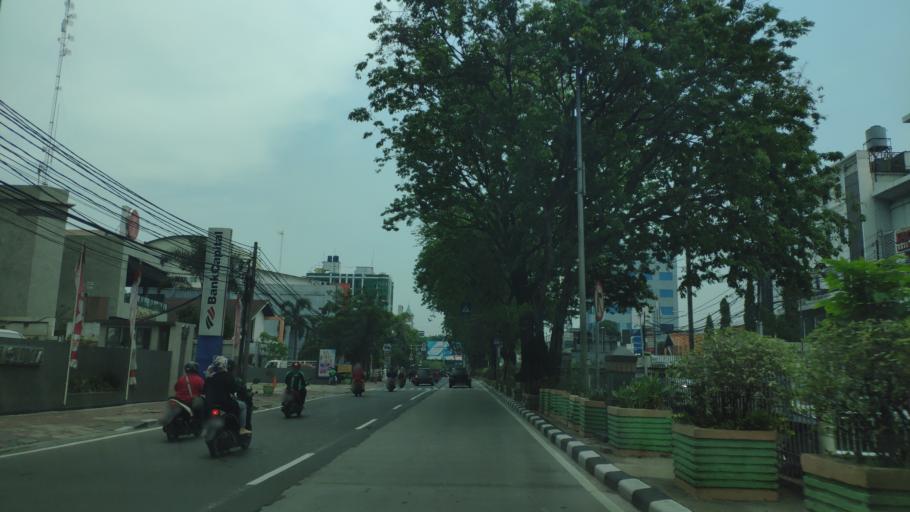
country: ID
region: Jakarta Raya
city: Jakarta
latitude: -6.1765
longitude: 106.8008
